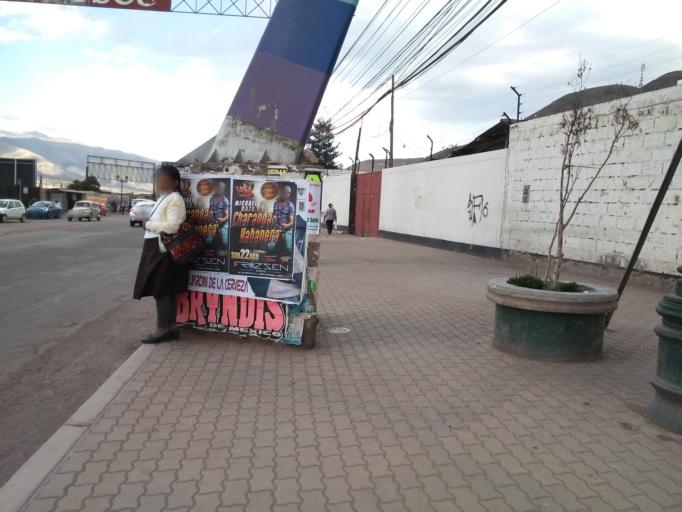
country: PE
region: Cusco
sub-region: Provincia de Cusco
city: Cusco
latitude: -13.5389
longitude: -71.9456
